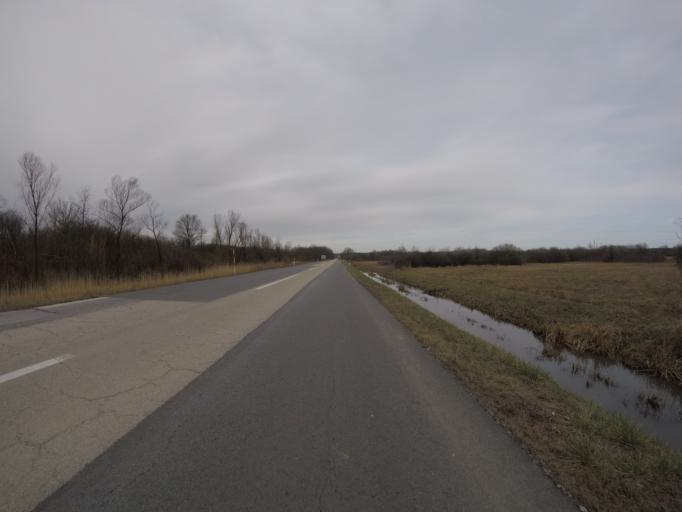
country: HR
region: Grad Zagreb
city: Horvati
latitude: 45.5592
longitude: 15.8608
